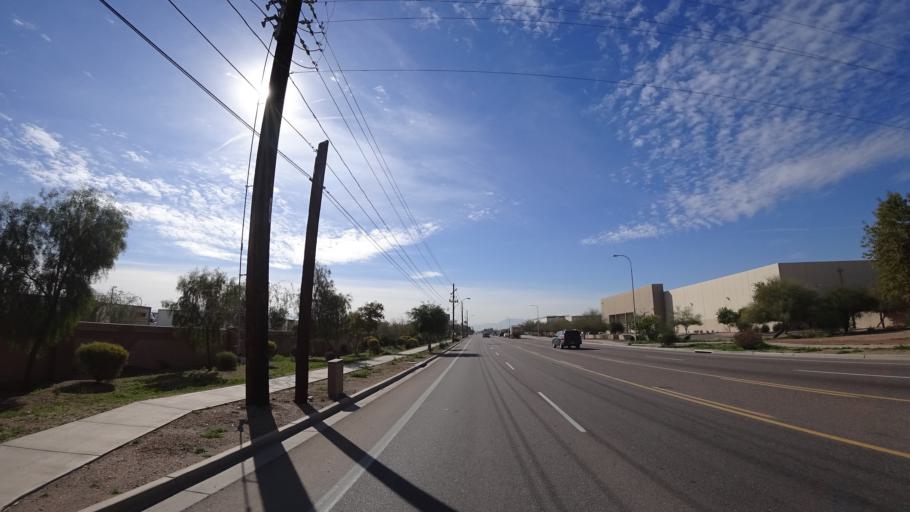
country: US
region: Arizona
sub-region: Maricopa County
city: Laveen
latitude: 33.4298
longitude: -112.1692
